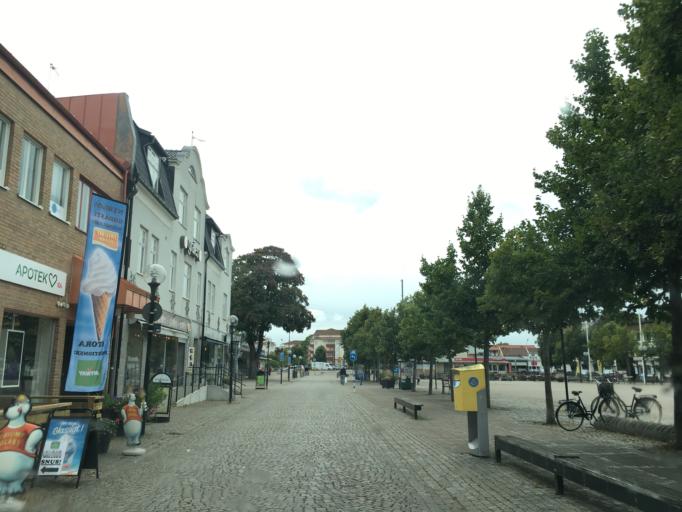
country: SE
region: Kalmar
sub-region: Nybro Kommun
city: Nybro
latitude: 56.7442
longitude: 15.9078
